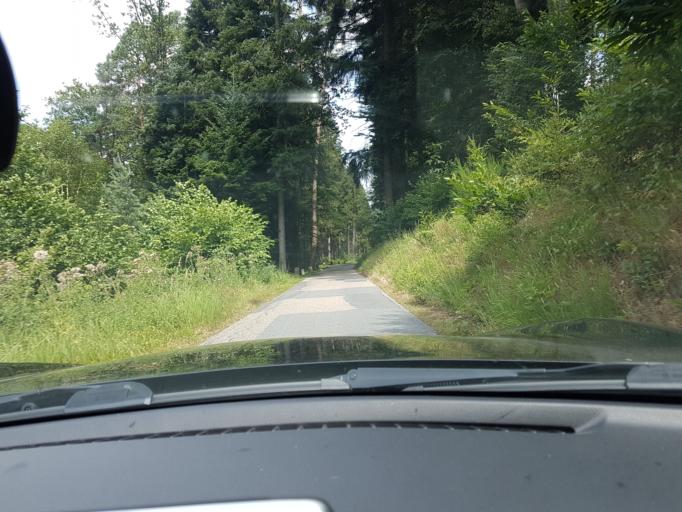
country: DE
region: Hesse
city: Hirschhorn
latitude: 49.4543
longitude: 8.8977
